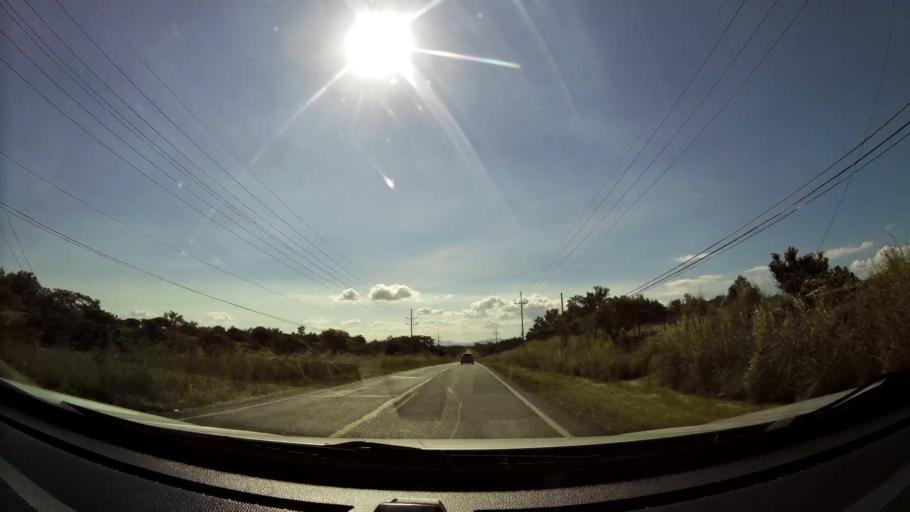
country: CR
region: Guanacaste
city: Liberia
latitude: 10.6073
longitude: -85.5061
